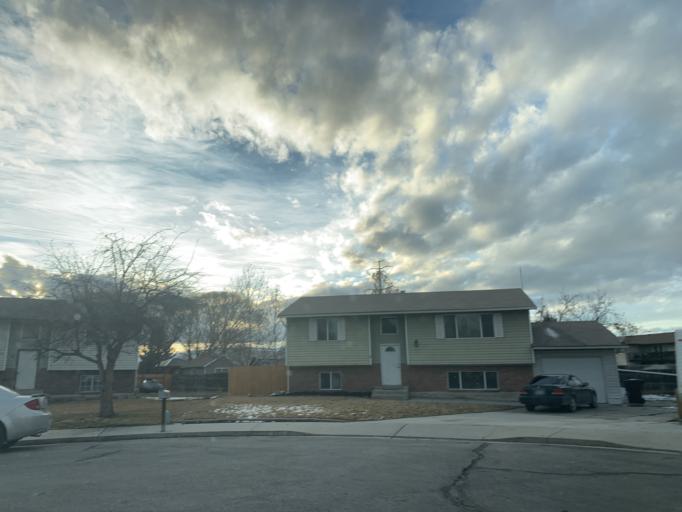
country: US
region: Utah
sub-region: Utah County
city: Provo
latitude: 40.2448
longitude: -111.7010
